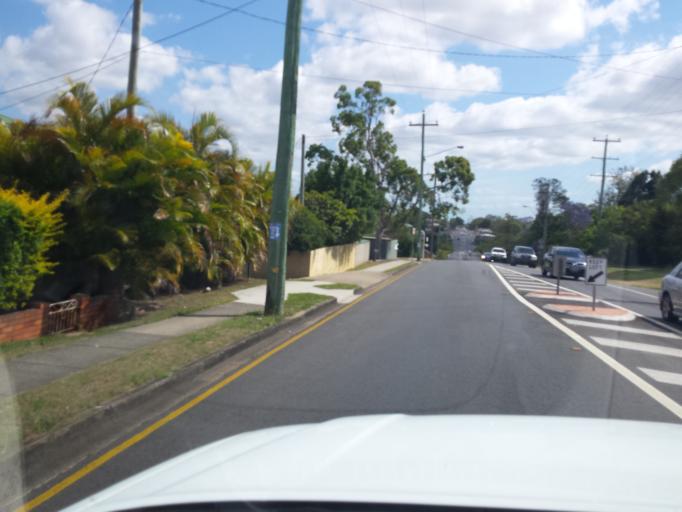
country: AU
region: Queensland
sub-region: Brisbane
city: Zillmere
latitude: -27.3717
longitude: 153.0358
